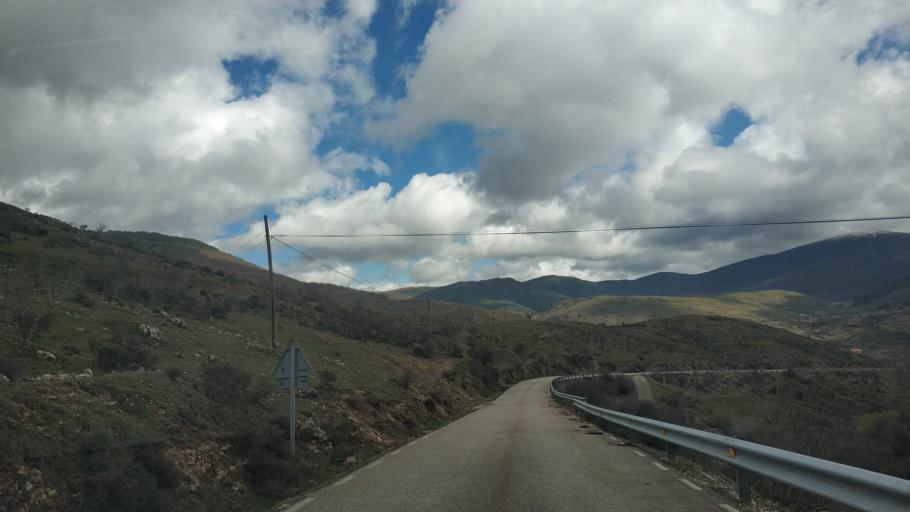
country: ES
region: Castille and Leon
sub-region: Provincia de Burgos
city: Neila
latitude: 42.0576
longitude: -3.0056
